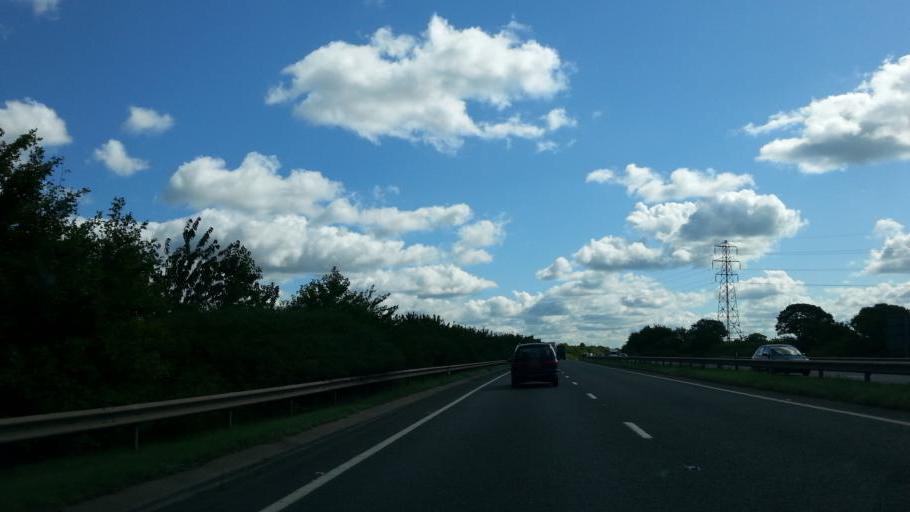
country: GB
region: England
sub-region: Derbyshire
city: Findern
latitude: 52.8705
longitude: -1.5221
